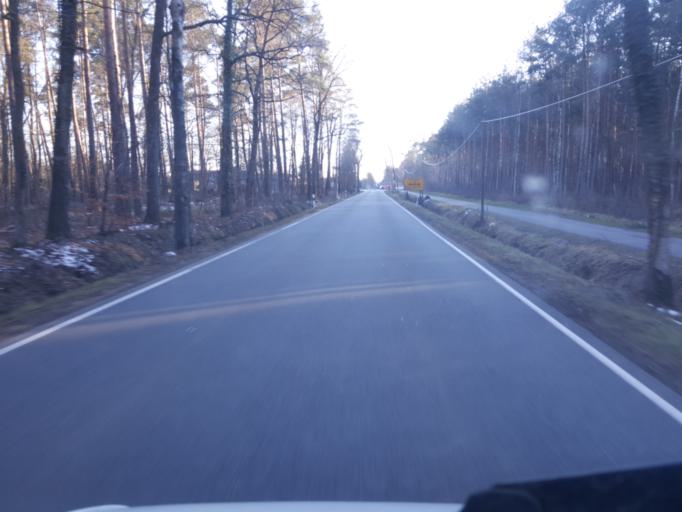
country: DE
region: North Rhine-Westphalia
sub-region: Regierungsbezirk Detmold
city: Hille
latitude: 52.3973
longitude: 8.7069
